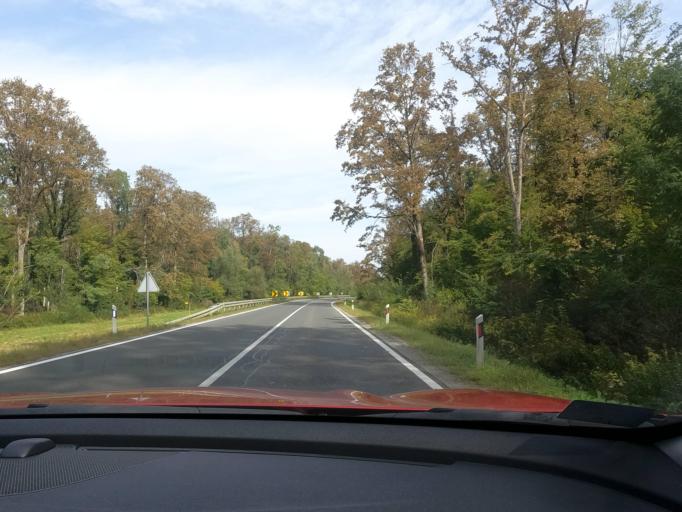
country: HR
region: Sisacko-Moslavacka
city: Budasevo
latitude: 45.4959
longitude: 16.5095
